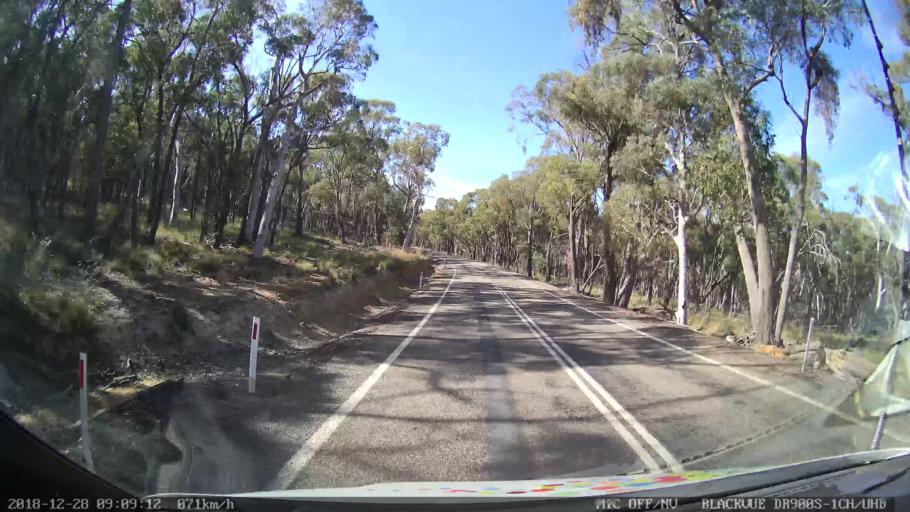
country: AU
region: New South Wales
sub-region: Upper Lachlan Shire
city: Crookwell
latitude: -34.2190
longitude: 149.3354
